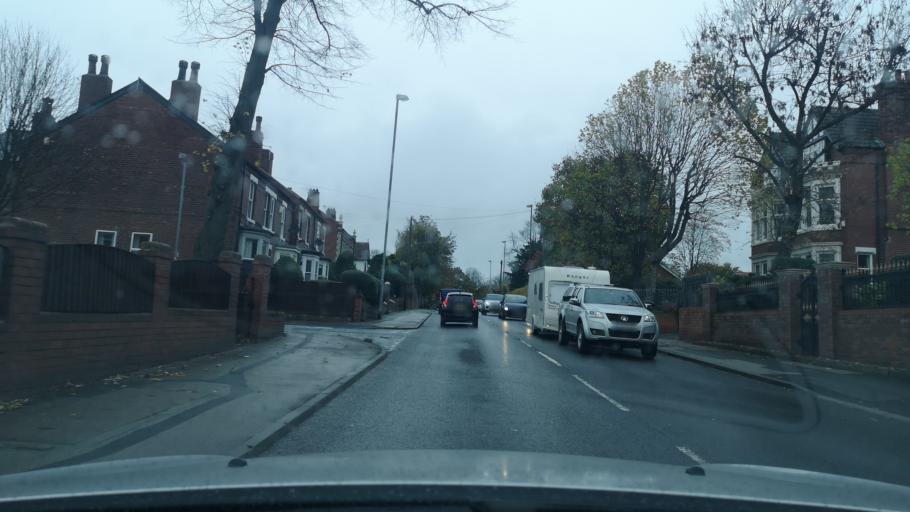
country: GB
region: England
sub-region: City and Borough of Wakefield
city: Pontefract
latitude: 53.6818
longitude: -1.3132
